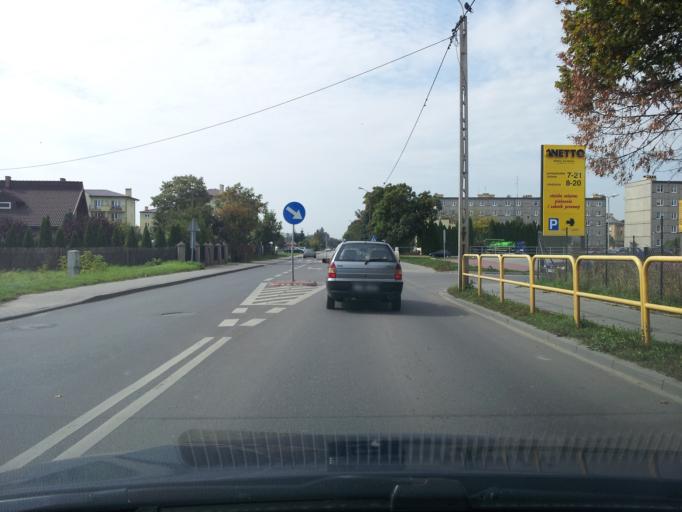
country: PL
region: Kujawsko-Pomorskie
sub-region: Powiat rypinski
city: Rypin
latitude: 53.0656
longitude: 19.4258
